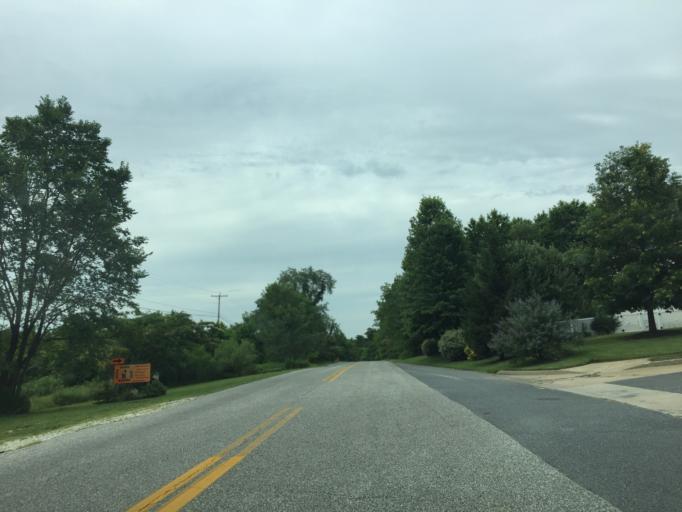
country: US
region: Maryland
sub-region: Baltimore County
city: Edgemere
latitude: 39.2578
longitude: -76.4555
